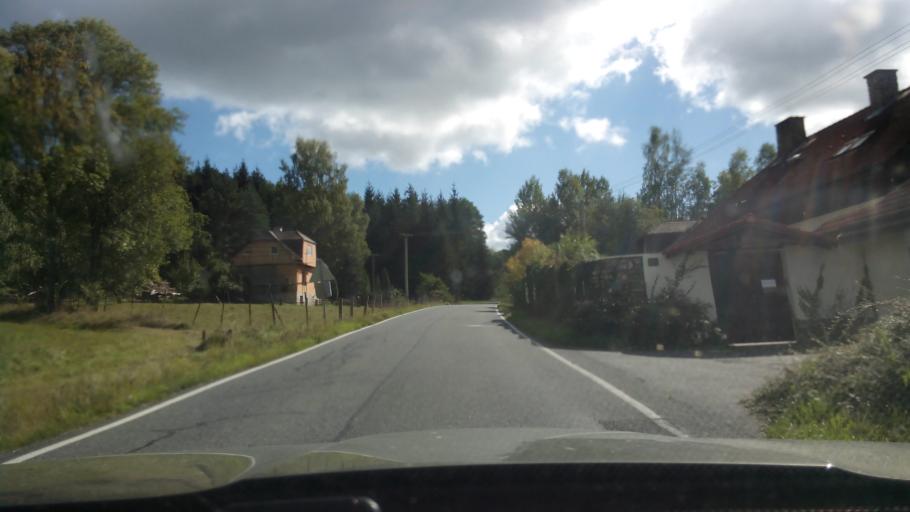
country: CZ
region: Plzensky
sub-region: Okres Klatovy
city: Kasperske Hory
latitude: 49.1453
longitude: 13.5723
